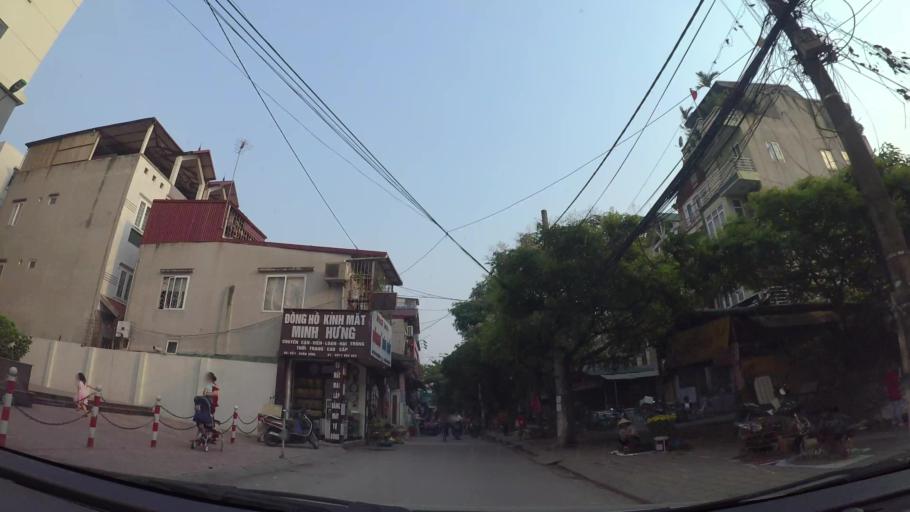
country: VN
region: Ha Noi
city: Tay Ho
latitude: 21.0699
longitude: 105.7914
